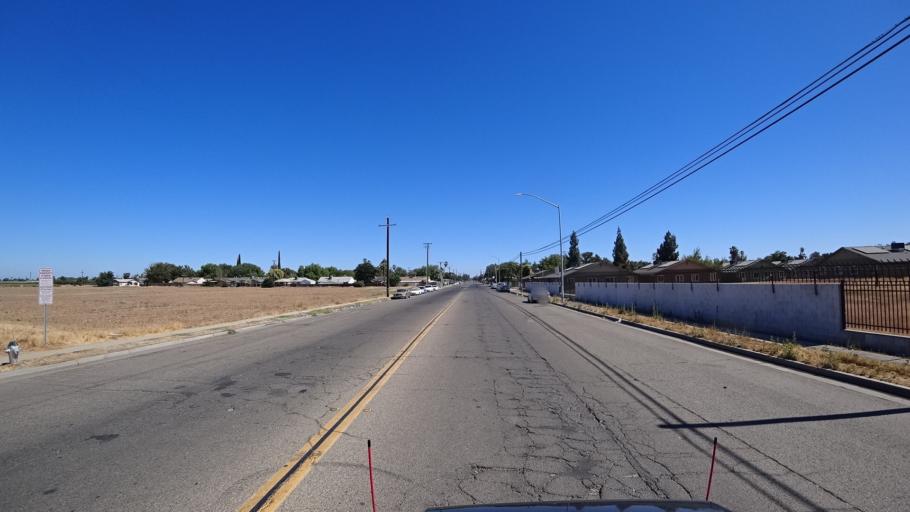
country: US
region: California
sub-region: Fresno County
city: West Park
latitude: 36.7020
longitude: -119.7998
